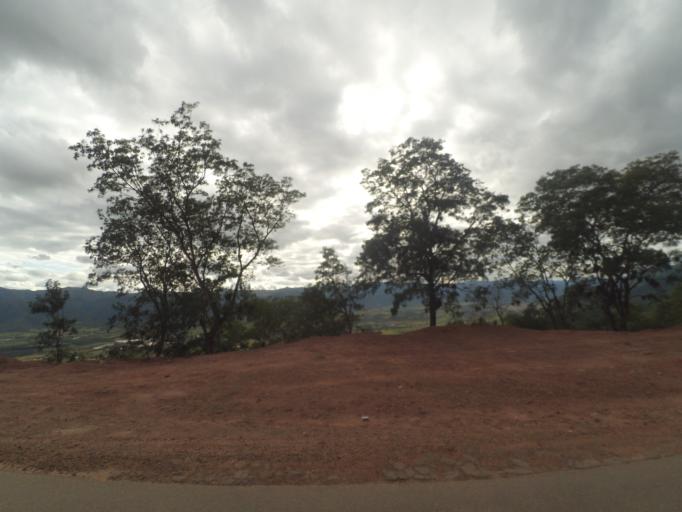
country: BO
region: Santa Cruz
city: Samaipata
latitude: -18.1646
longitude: -63.8918
